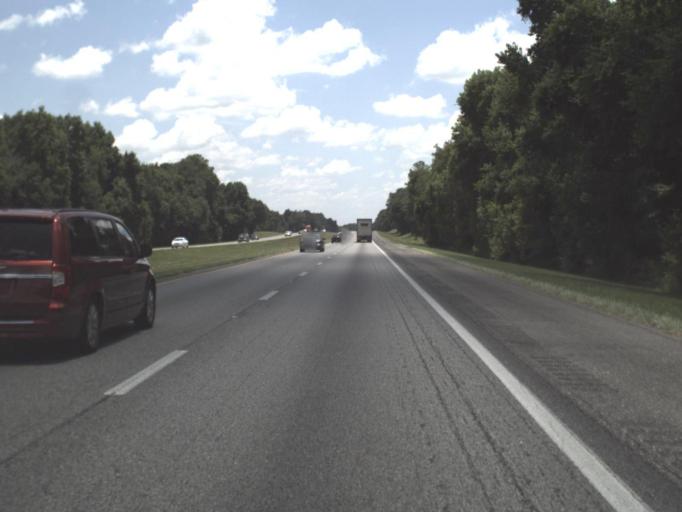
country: US
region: Florida
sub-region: Madison County
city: Madison
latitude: 30.4307
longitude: -83.5861
